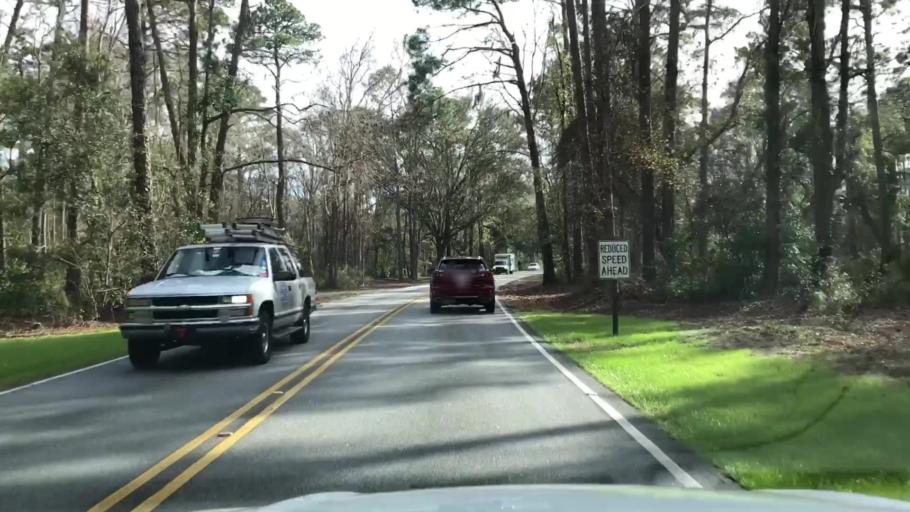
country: US
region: South Carolina
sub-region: Beaufort County
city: Hilton Head Island
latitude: 32.2253
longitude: -80.7234
